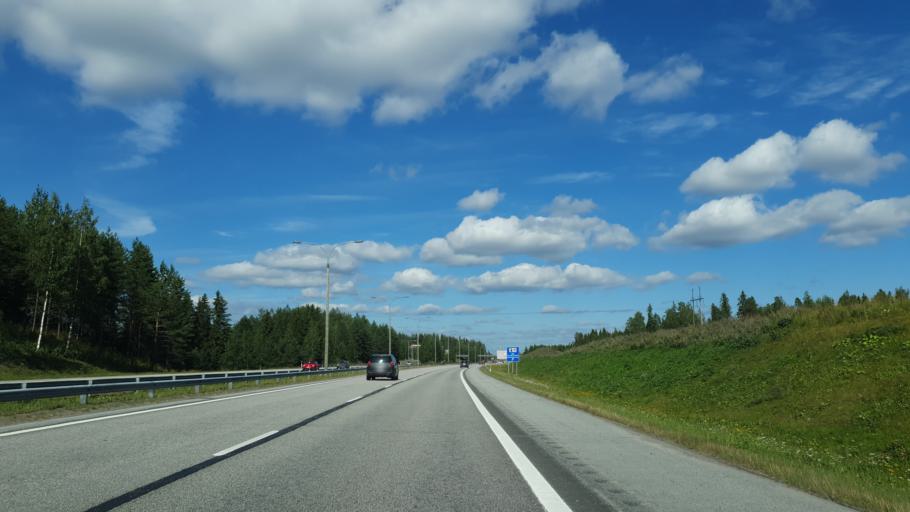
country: FI
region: Central Finland
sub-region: Jyvaeskylae
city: Muurame
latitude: 62.1846
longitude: 25.6871
